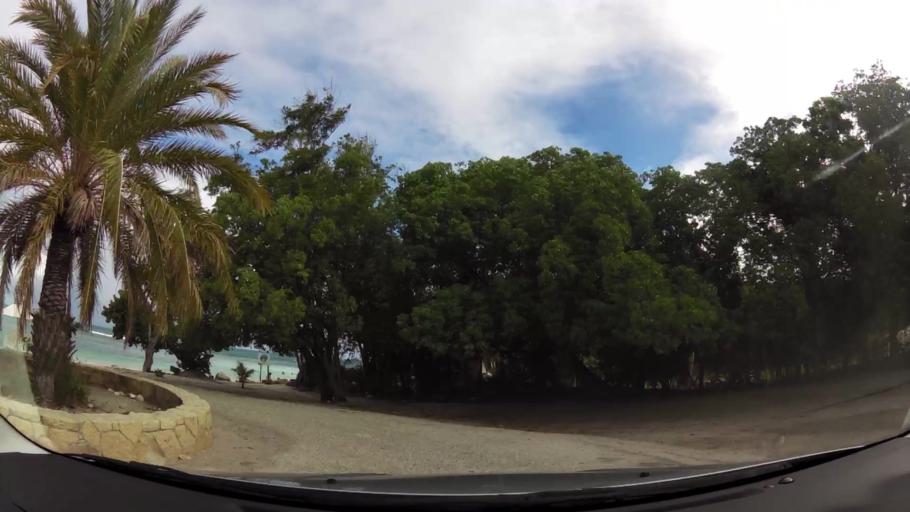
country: AG
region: Saint Peter
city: Parham
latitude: 17.0990
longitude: -61.6890
